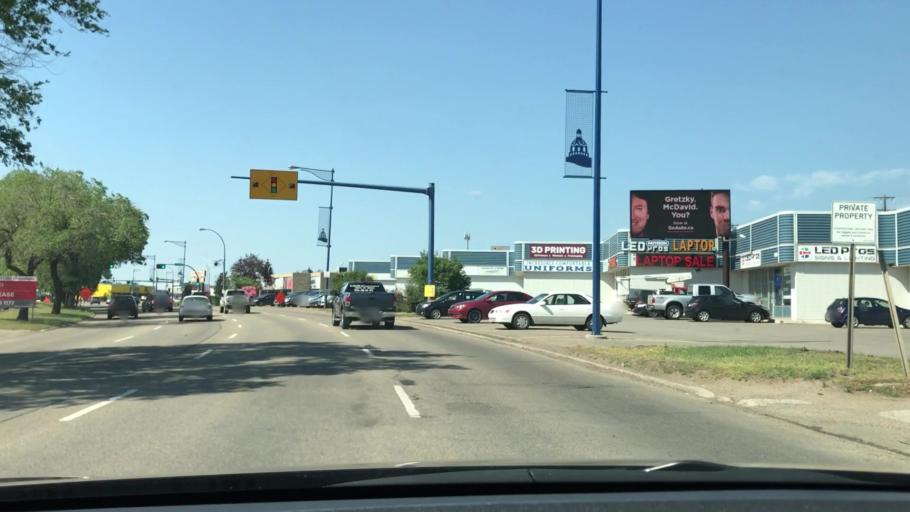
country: CA
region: Alberta
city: Edmonton
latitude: 53.4980
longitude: -113.4921
